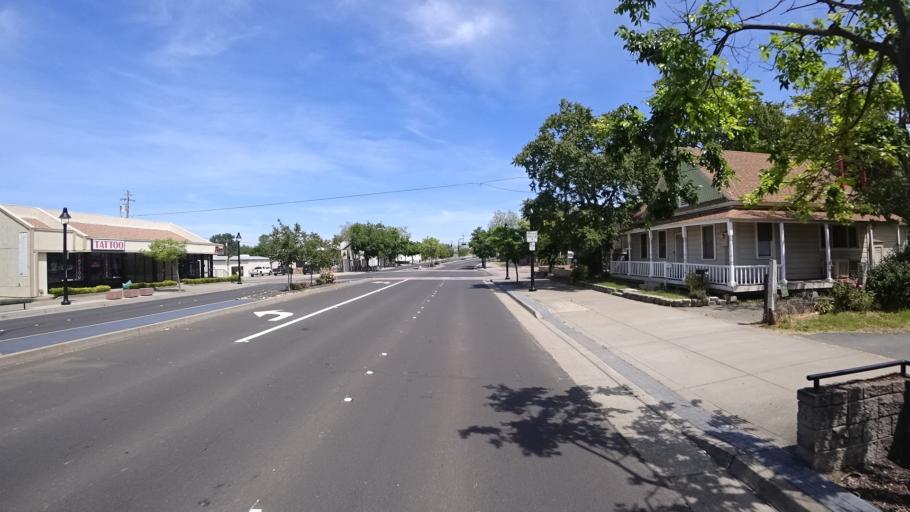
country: US
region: California
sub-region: Placer County
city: Rocklin
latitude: 38.7938
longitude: -121.2337
